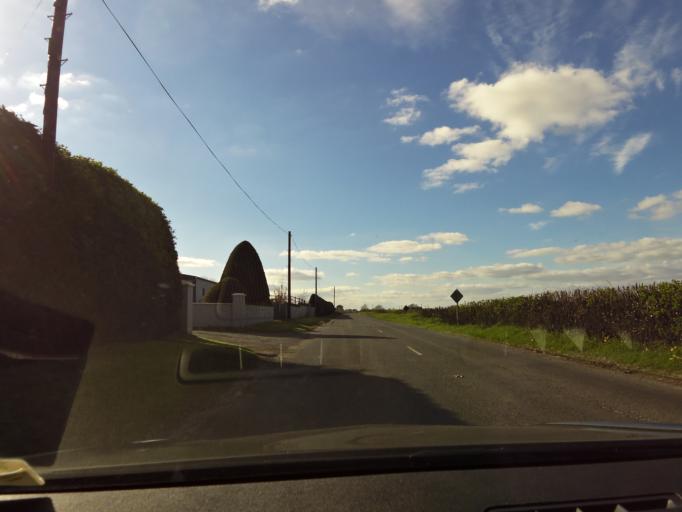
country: IE
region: Leinster
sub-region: Uibh Fhaili
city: Birr
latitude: 53.0962
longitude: -7.9701
